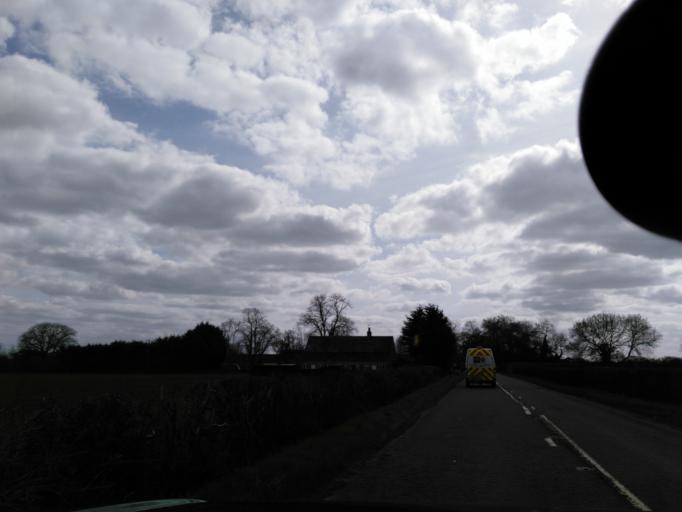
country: GB
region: England
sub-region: Wiltshire
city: Hankerton
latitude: 51.6491
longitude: -2.0576
